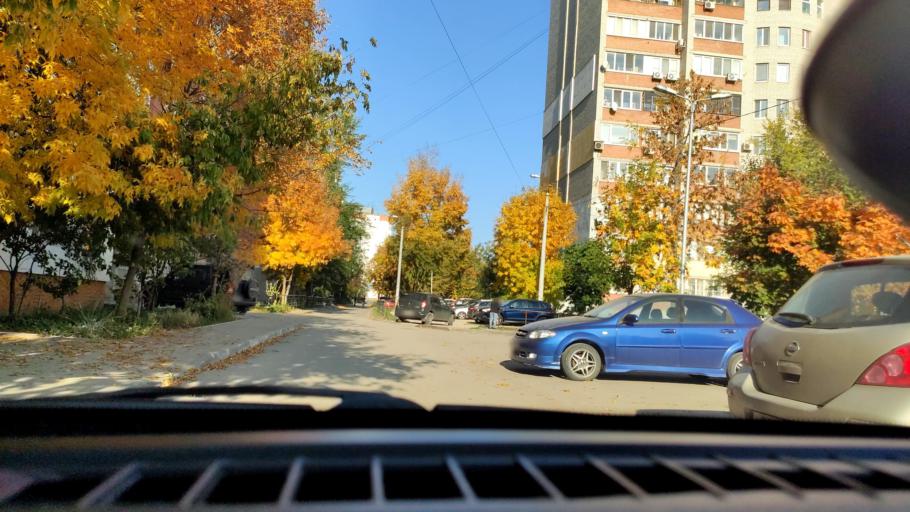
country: RU
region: Samara
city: Samara
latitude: 53.2564
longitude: 50.2352
